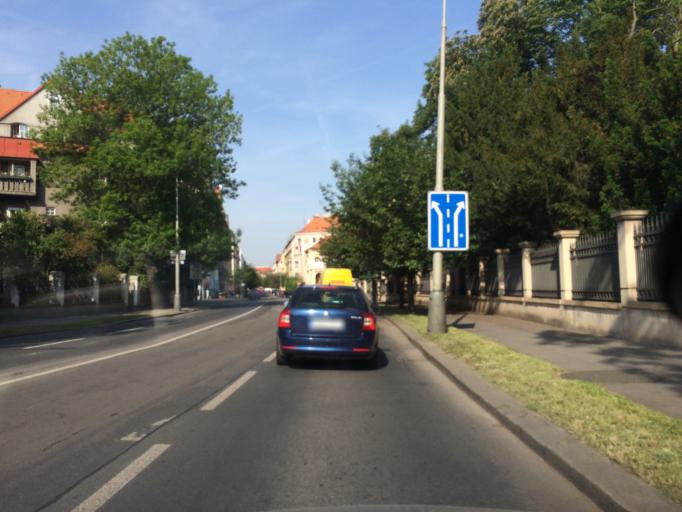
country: CZ
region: Praha
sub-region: Praha 1
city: Mala Strana
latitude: 50.0995
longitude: 14.4065
